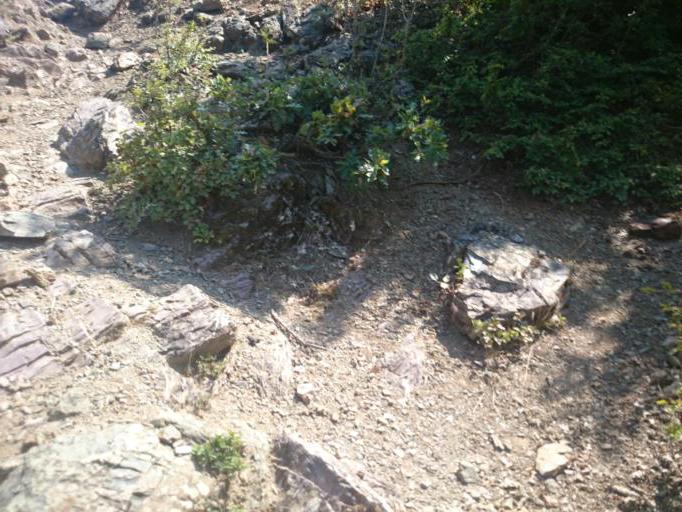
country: AL
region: Diber
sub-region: Rrethi i Dibres
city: Melan
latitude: 41.6183
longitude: 20.4125
